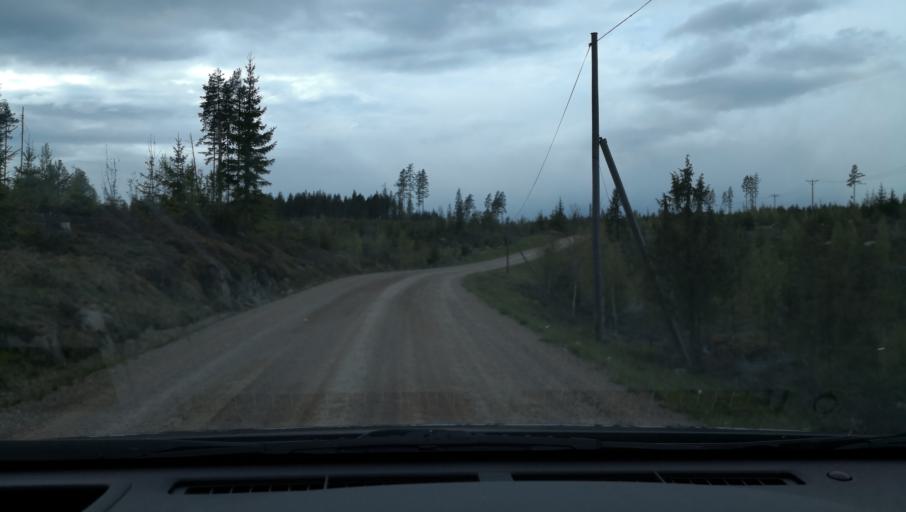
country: SE
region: Vaestmanland
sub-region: Fagersta Kommun
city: Fagersta
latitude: 60.1205
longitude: 15.7781
